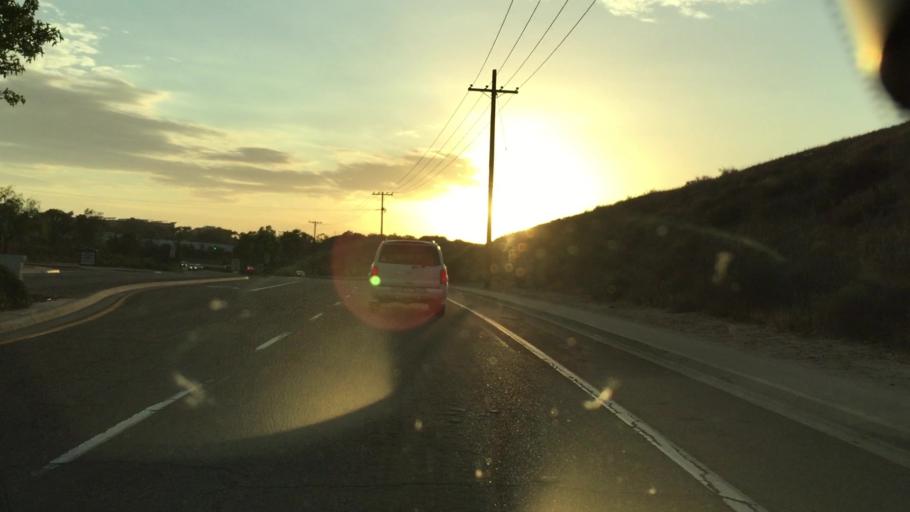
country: US
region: California
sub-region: San Diego County
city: La Mesa
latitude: 32.8335
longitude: -117.1150
